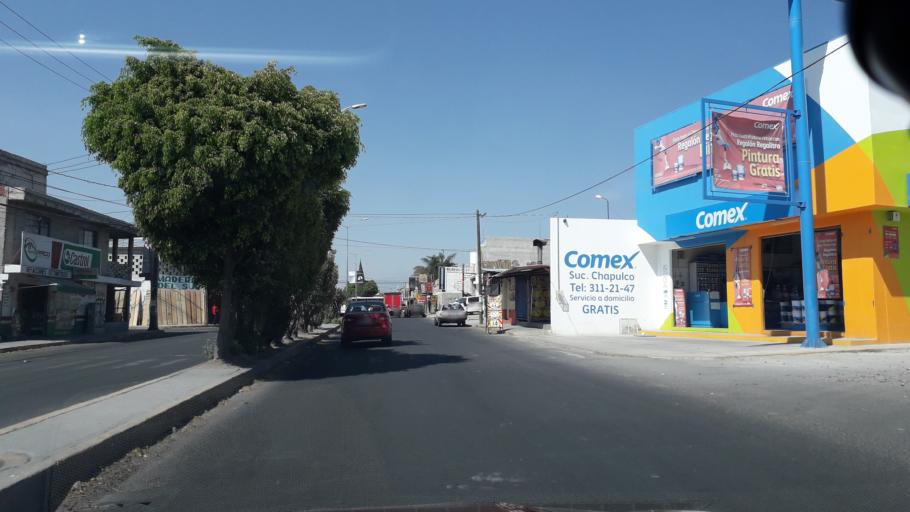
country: MX
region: Puebla
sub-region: Puebla
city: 18 de Marzo
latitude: 18.9863
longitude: -98.2163
